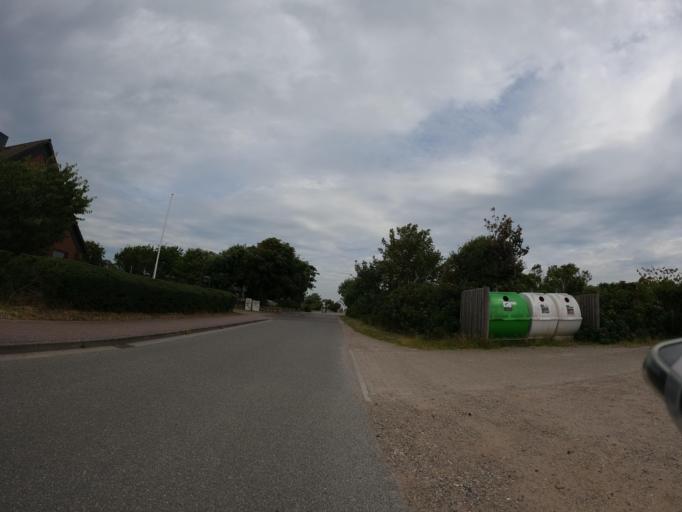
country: DE
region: Schleswig-Holstein
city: Westerland
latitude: 54.9323
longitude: 8.3268
